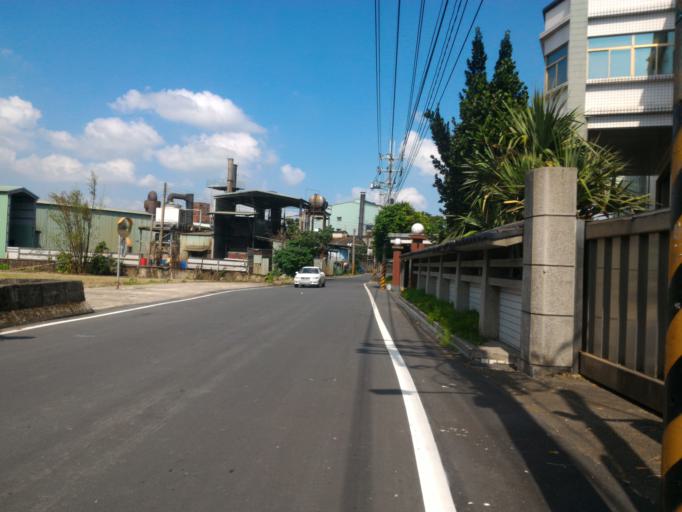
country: TW
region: Taiwan
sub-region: Taoyuan
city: Taoyuan
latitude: 24.9606
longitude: 121.3996
